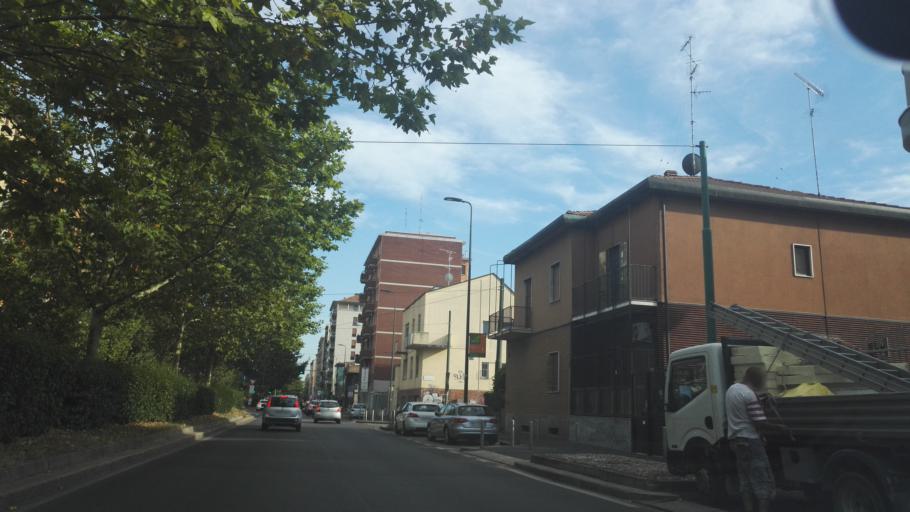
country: IT
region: Lombardy
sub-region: Citta metropolitana di Milano
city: Romano Banco
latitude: 45.4586
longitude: 9.1505
